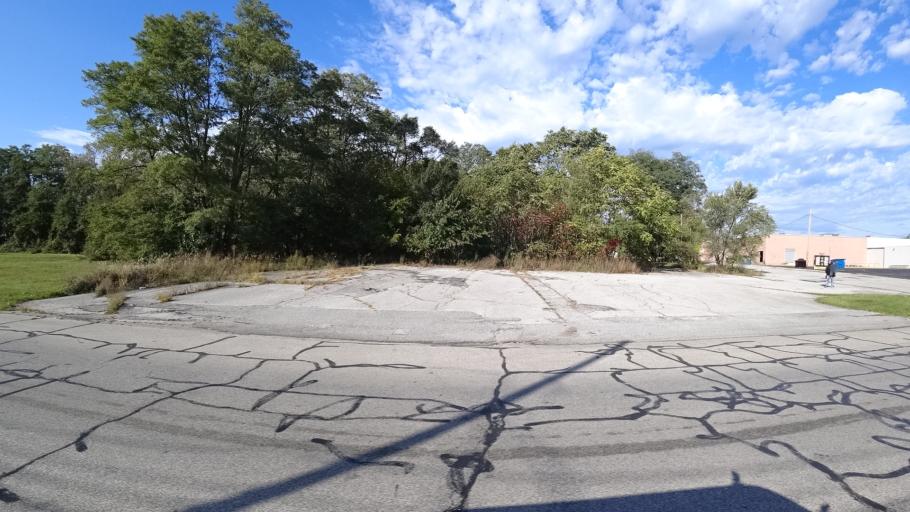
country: US
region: Indiana
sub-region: LaPorte County
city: Trail Creek
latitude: 41.7071
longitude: -86.8697
